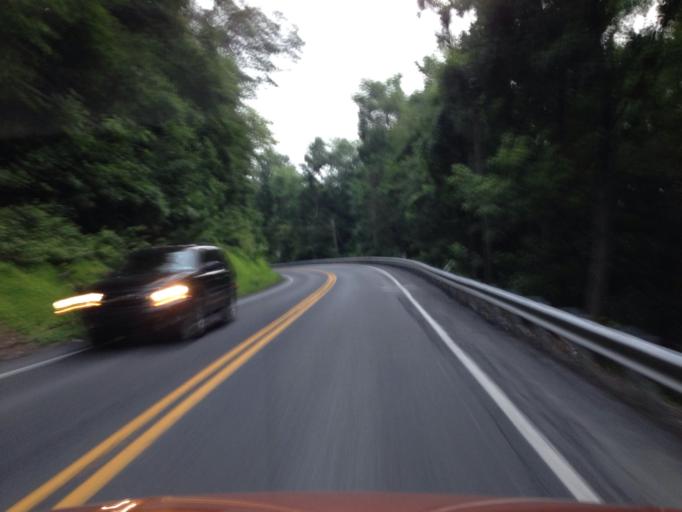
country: US
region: Pennsylvania
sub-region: Lancaster County
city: Rothsville
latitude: 40.1469
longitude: -76.2752
